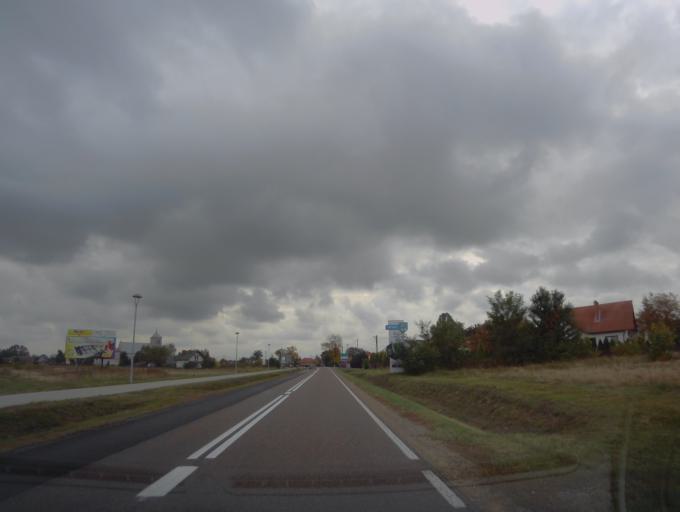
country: PL
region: Subcarpathian Voivodeship
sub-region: Powiat nizanski
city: Krzeszow
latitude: 50.3721
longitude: 22.3140
